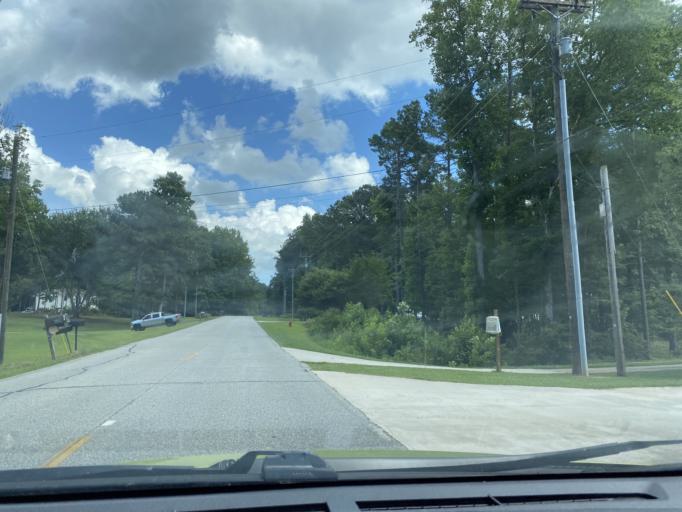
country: US
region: Georgia
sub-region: Fulton County
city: Palmetto
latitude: 33.4196
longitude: -84.6993
